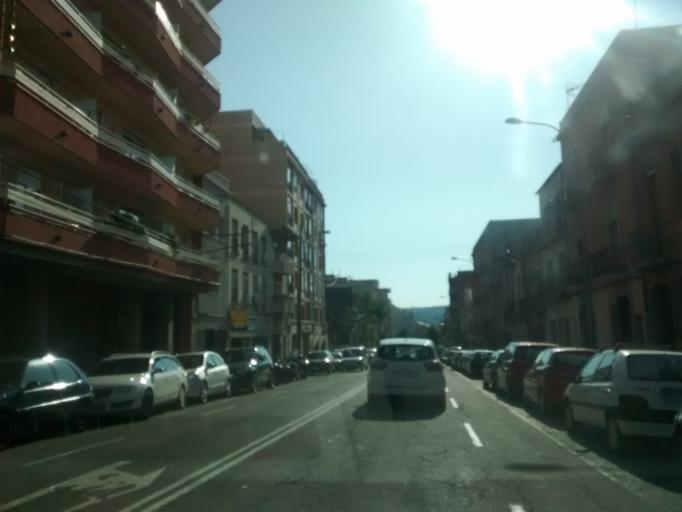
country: ES
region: Catalonia
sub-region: Provincia de Barcelona
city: Sant Feliu de Llobregat
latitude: 41.3795
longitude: 2.0508
